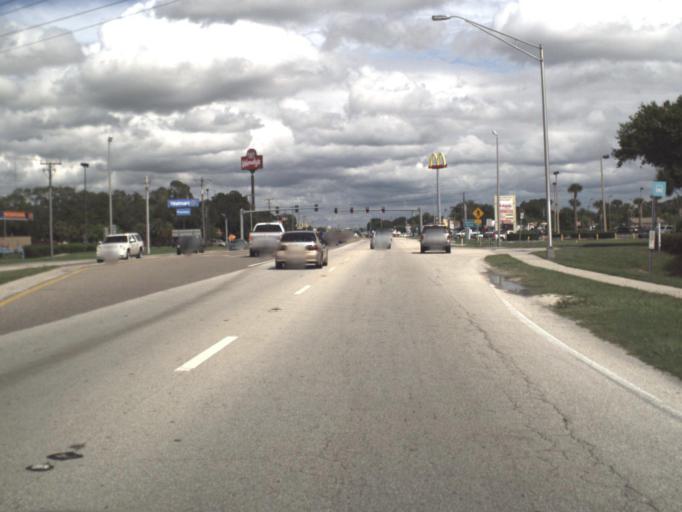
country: US
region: Florida
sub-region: Manatee County
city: Palmetto
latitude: 27.5211
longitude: -82.5614
